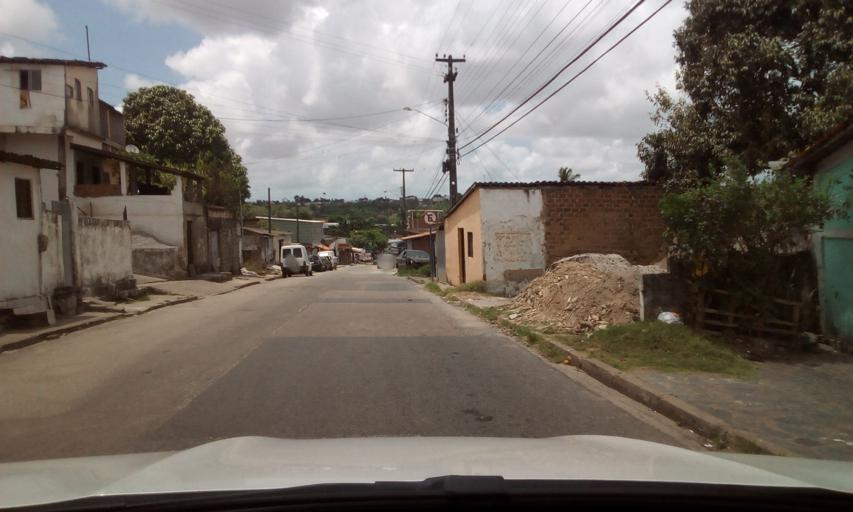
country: BR
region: Paraiba
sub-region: Joao Pessoa
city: Joao Pessoa
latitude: -7.1263
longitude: -34.8911
